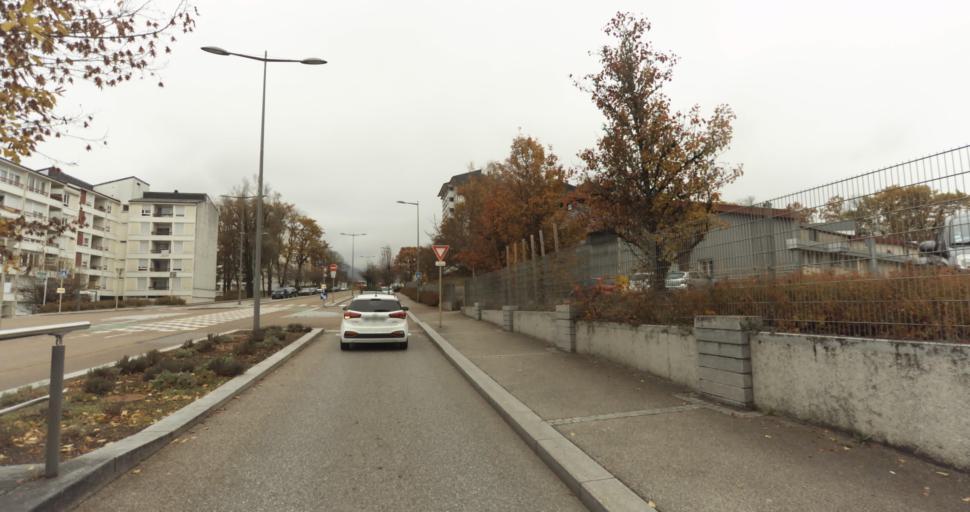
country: FR
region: Rhone-Alpes
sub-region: Departement de la Haute-Savoie
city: Cran-Gevrier
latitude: 45.8926
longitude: 6.1013
